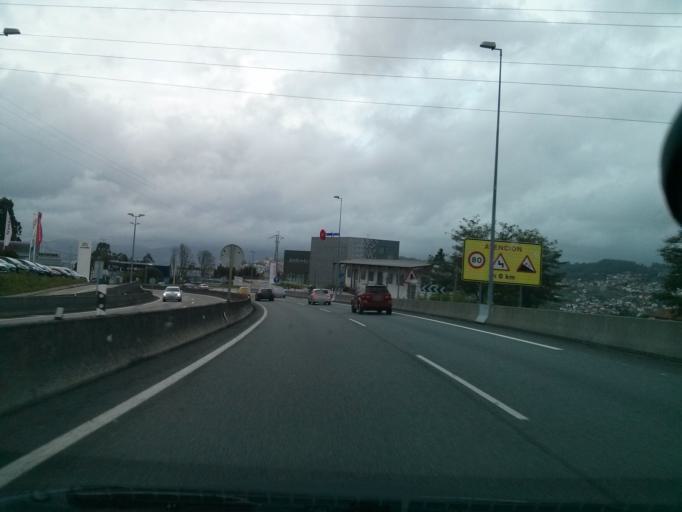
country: ES
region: Galicia
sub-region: Provincia de Pontevedra
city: Vigo
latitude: 42.2134
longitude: -8.6719
